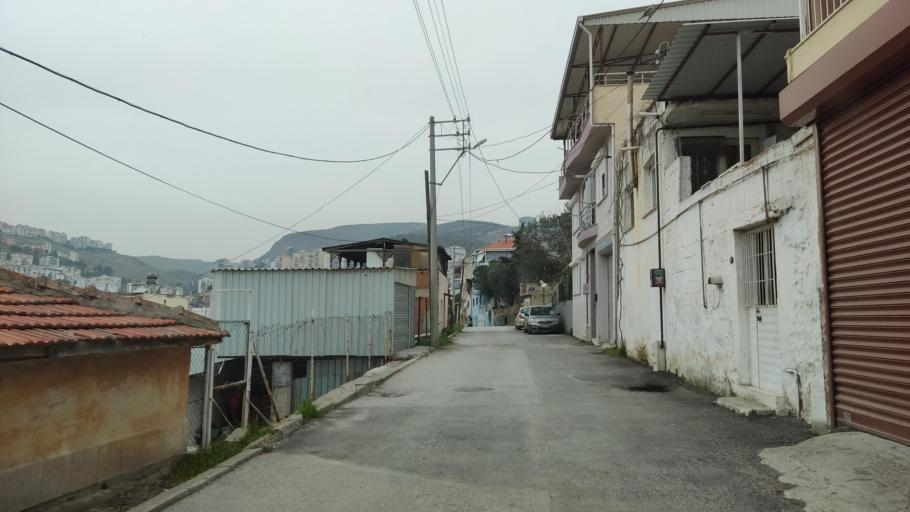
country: TR
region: Izmir
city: Karsiyaka
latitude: 38.4958
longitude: 27.0678
